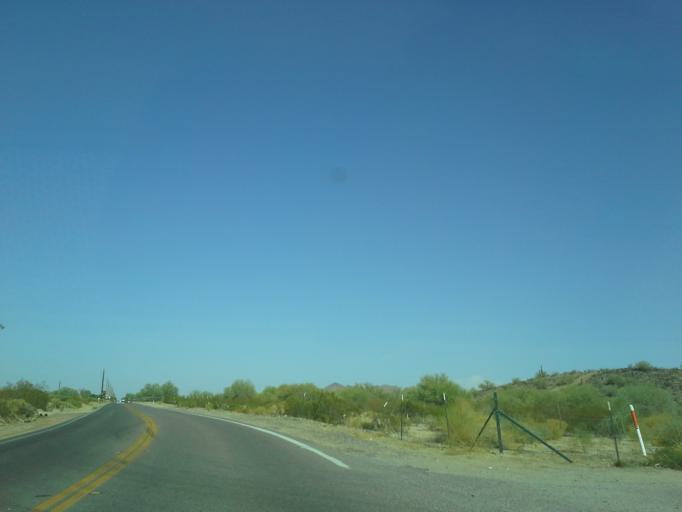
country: US
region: Arizona
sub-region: Maricopa County
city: Queen Creek
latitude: 33.2047
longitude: -111.7172
